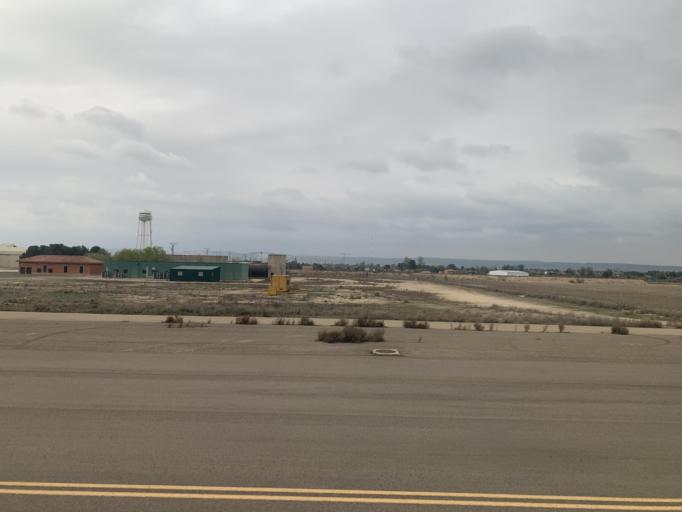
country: ES
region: Aragon
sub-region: Provincia de Zaragoza
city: Utebo
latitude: 41.6653
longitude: -1.0243
